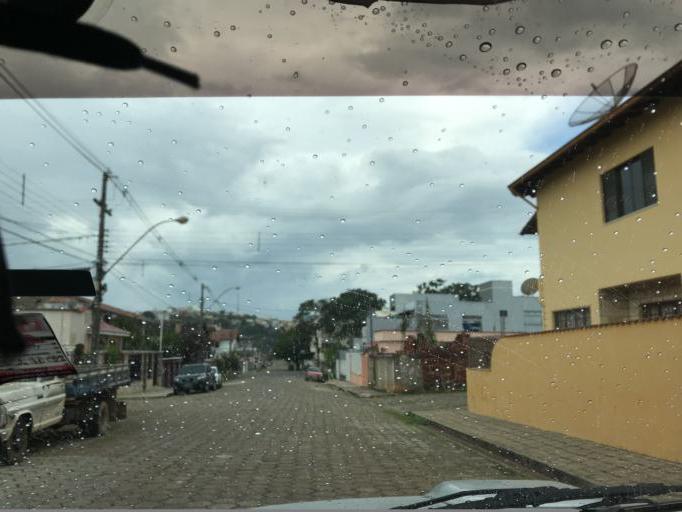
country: BR
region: Minas Gerais
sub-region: Tres Coracoes
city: Tres Coracoes
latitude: -21.7043
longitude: -45.2516
